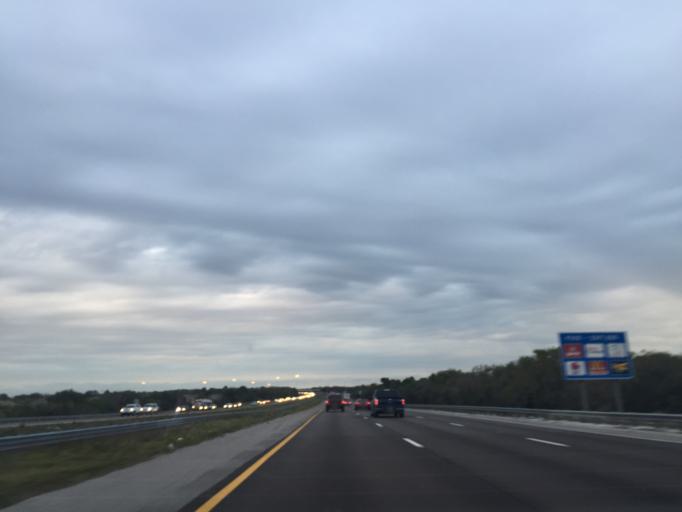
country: US
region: Florida
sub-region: Hillsborough County
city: Riverview
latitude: 27.8372
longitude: -82.3490
